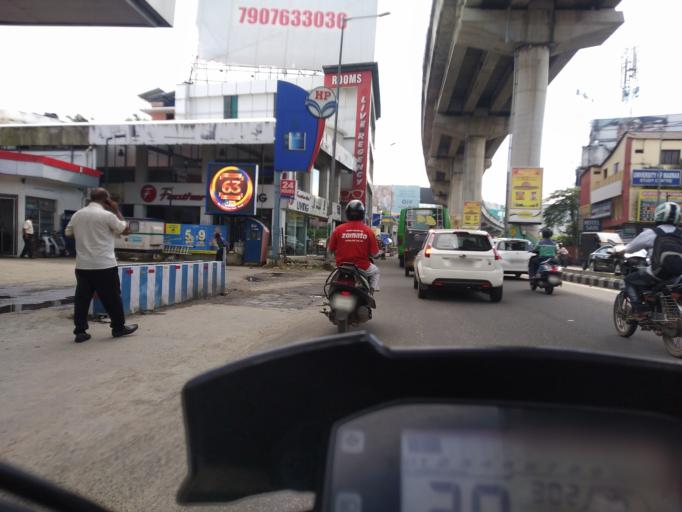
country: IN
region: Kerala
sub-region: Ernakulam
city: Cochin
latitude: 9.9881
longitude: 76.2858
